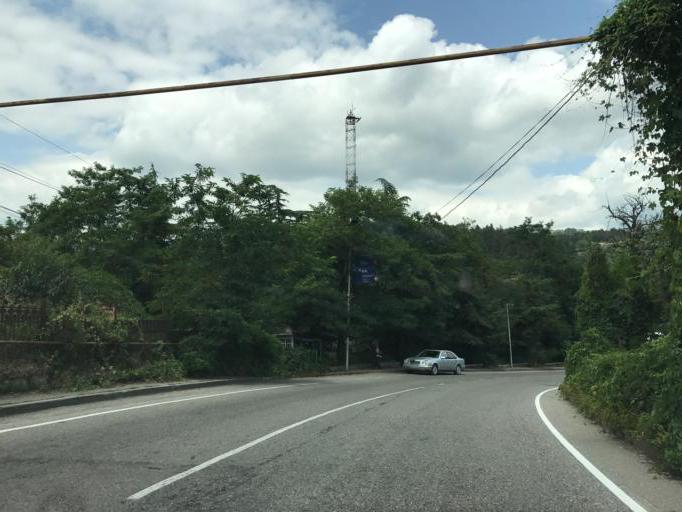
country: AM
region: Tavush
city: Dilijan
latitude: 40.7379
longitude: 44.8642
